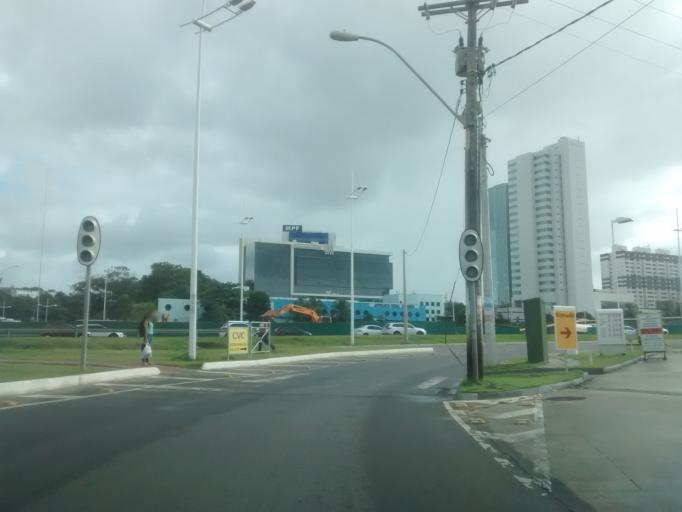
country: BR
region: Bahia
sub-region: Salvador
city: Salvador
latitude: -12.9690
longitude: -38.4387
